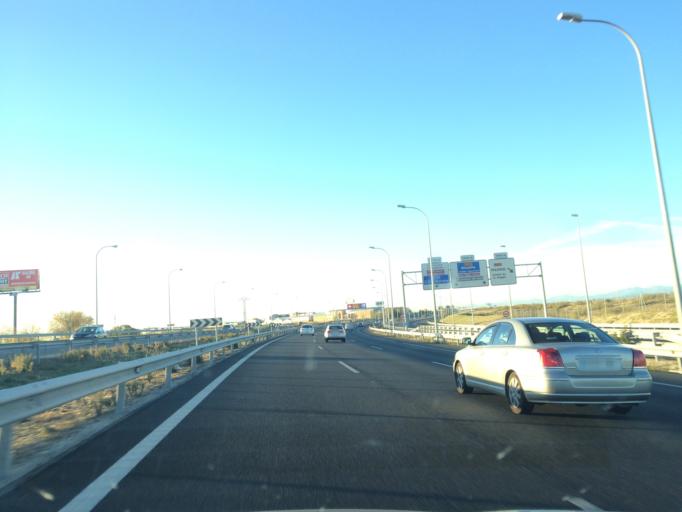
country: ES
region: Madrid
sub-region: Provincia de Madrid
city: Alcorcon
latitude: 40.3853
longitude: -3.8251
